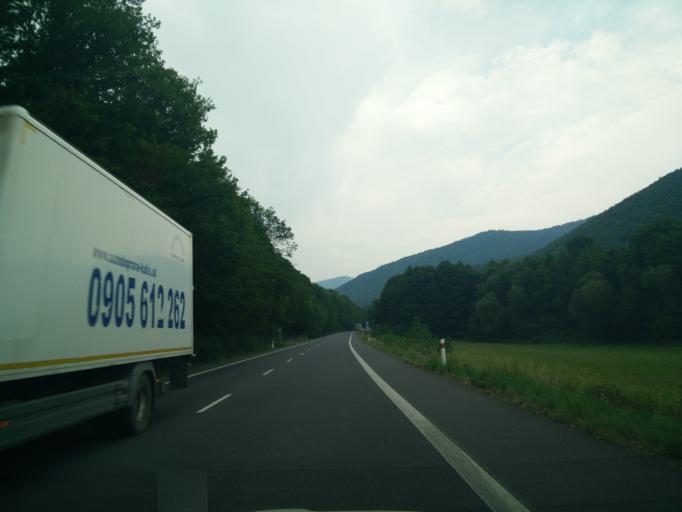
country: SK
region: Nitriansky
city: Handlova
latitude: 48.6473
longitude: 18.7622
